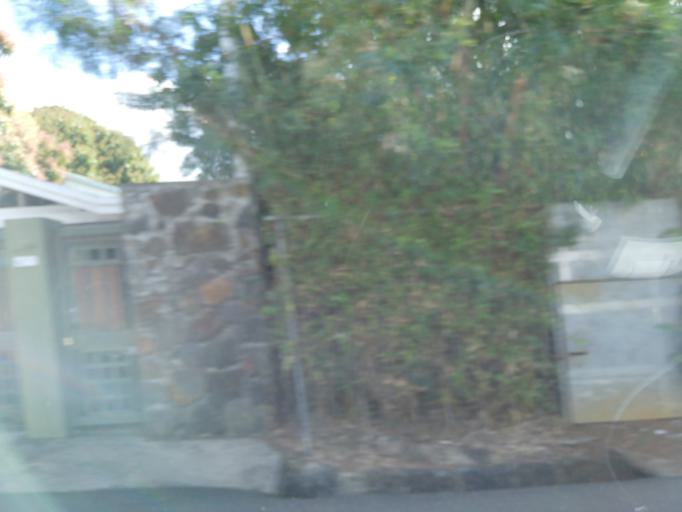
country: MU
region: Moka
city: Moka
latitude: -20.2274
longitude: 57.4745
